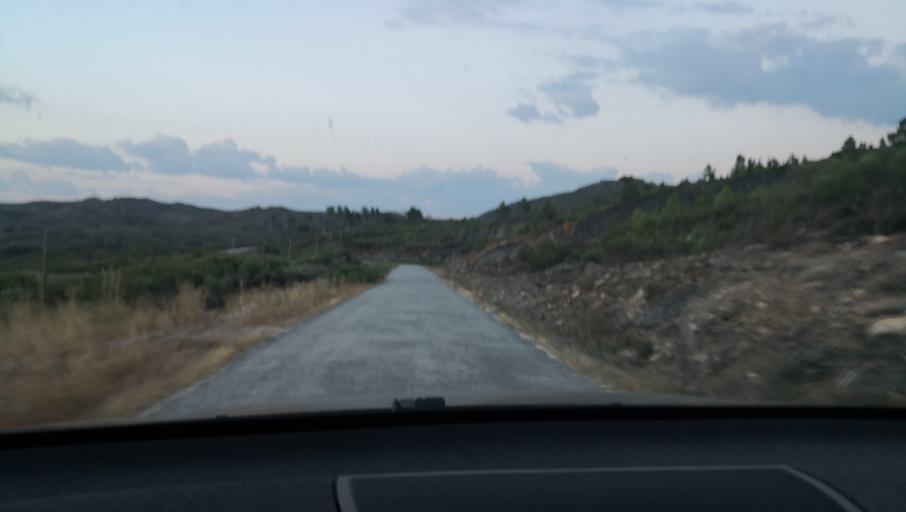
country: PT
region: Vila Real
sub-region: Sabrosa
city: Sabrosa
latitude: 41.2781
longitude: -7.6256
